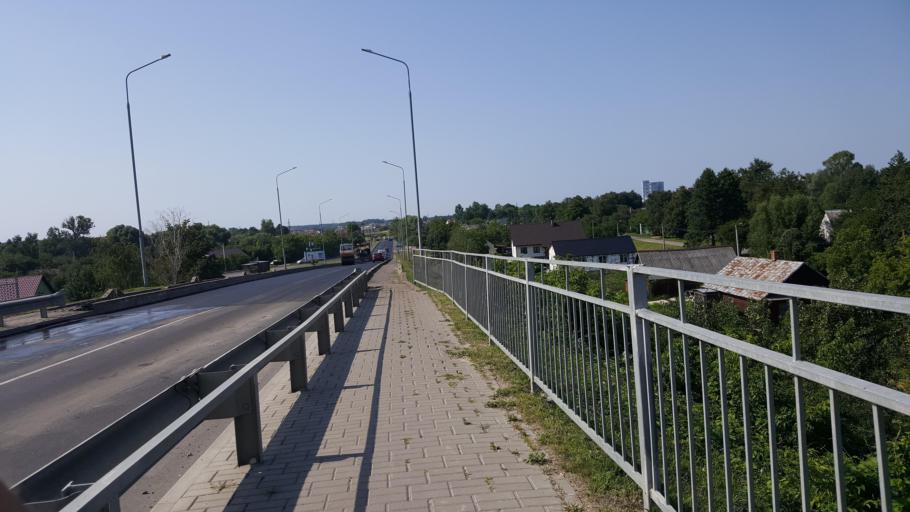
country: BY
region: Brest
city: Zhabinka
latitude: 52.1985
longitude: 24.0088
